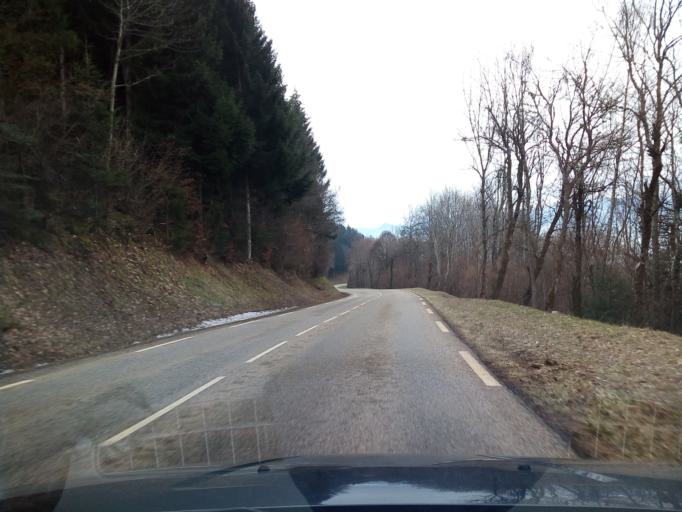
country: FR
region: Rhone-Alpes
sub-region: Departement de l'Isere
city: Revel
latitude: 45.1441
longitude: 5.8604
